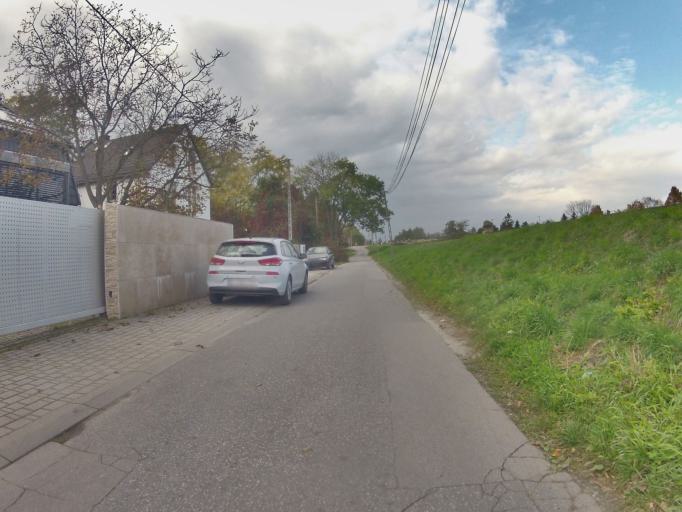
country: PL
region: Lesser Poland Voivodeship
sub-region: Krakow
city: Krakow
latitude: 50.0592
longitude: 19.9022
